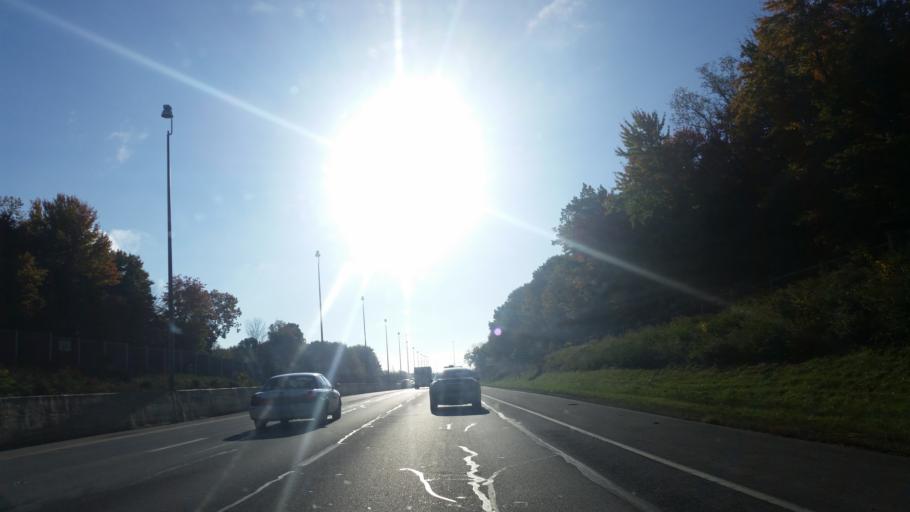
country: US
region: Ohio
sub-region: Summit County
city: Fairlawn
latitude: 41.1088
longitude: -81.6041
